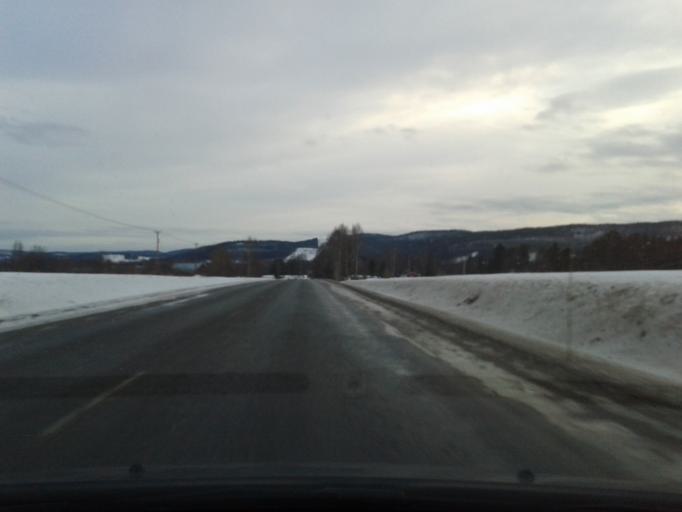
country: SE
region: Vaesternorrland
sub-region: Solleftea Kommun
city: Solleftea
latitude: 63.2485
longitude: 17.2110
